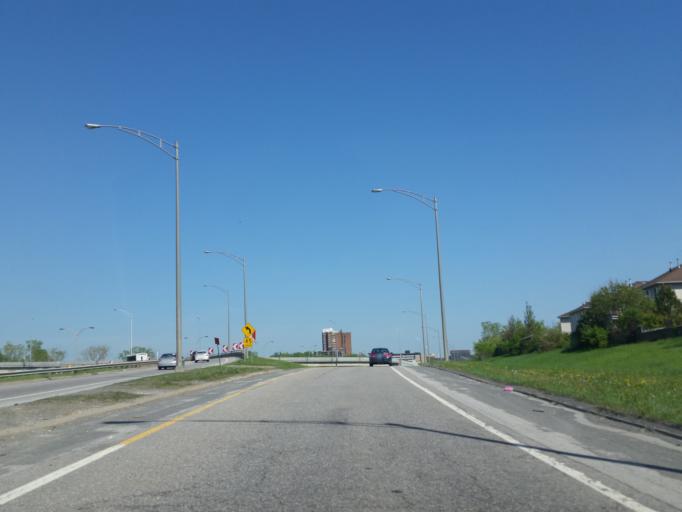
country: CA
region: Ontario
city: Ottawa
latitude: 45.4407
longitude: -75.7229
